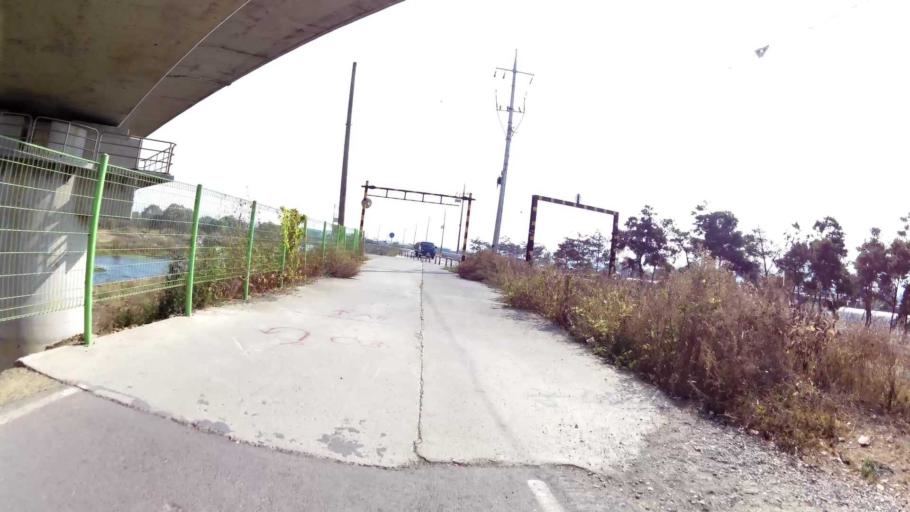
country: KR
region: Gyeongsangbuk-do
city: Gyeongsan-si
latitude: 35.8535
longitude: 128.7311
